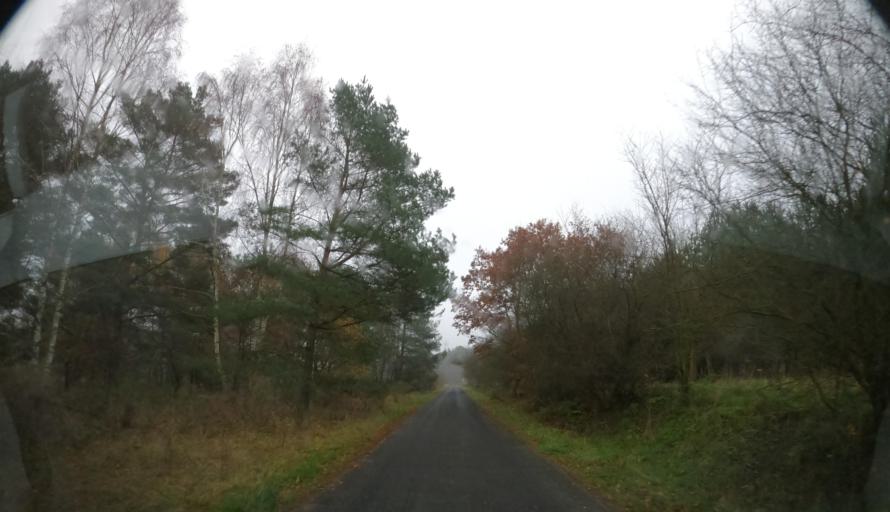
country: PL
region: West Pomeranian Voivodeship
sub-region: Powiat lobeski
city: Radowo Male
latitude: 53.6711
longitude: 15.4791
